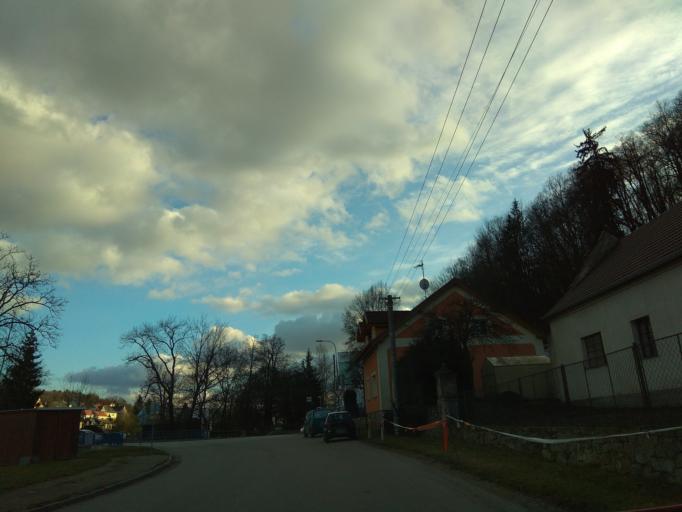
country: CZ
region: Jihocesky
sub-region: Okres Ceske Budejovice
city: Hluboka nad Vltavou
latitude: 49.0543
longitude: 14.4431
